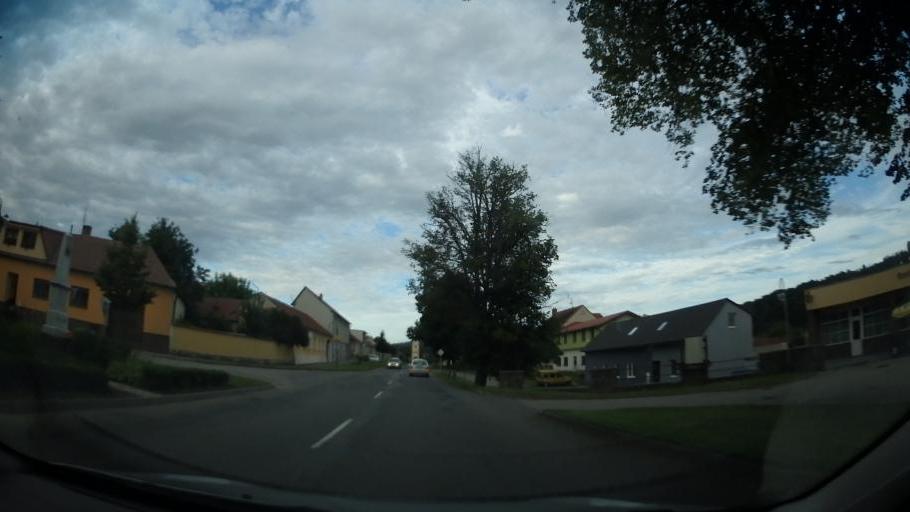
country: CZ
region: South Moravian
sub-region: Okres Blansko
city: Boskovice
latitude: 49.5395
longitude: 16.6942
